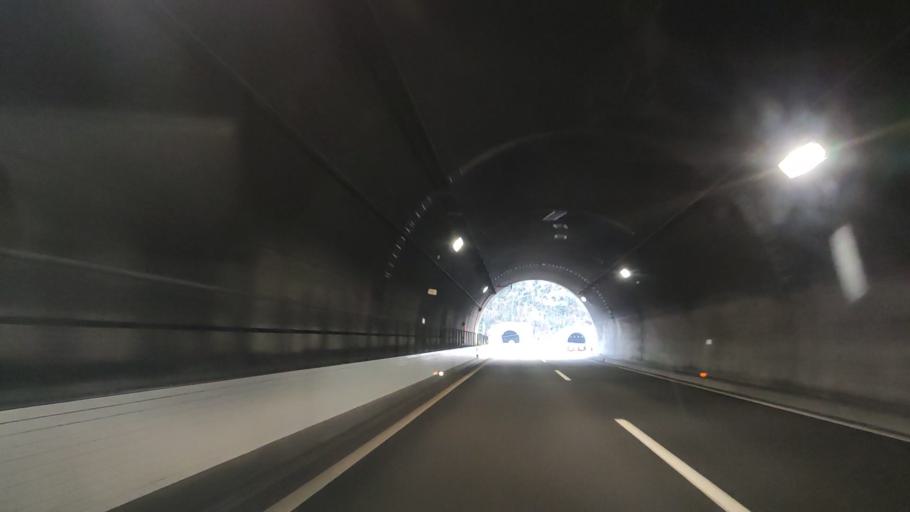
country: JP
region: Ehime
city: Saijo
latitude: 33.8471
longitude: 132.9950
